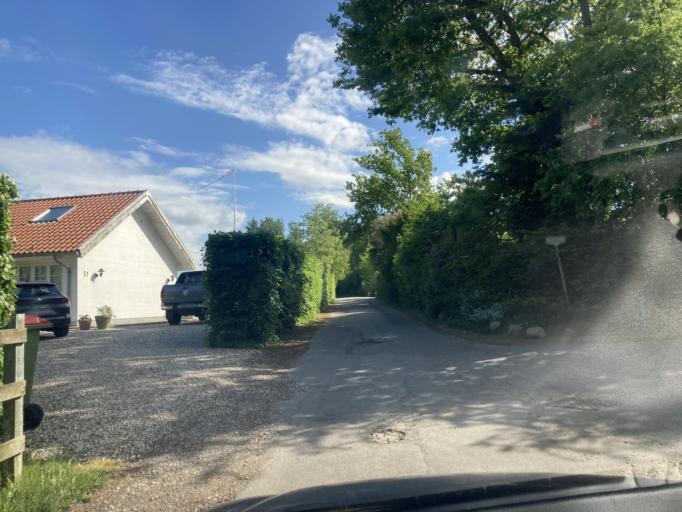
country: DK
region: Capital Region
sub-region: Gribskov Kommune
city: Helsinge
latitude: 56.0038
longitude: 12.1099
